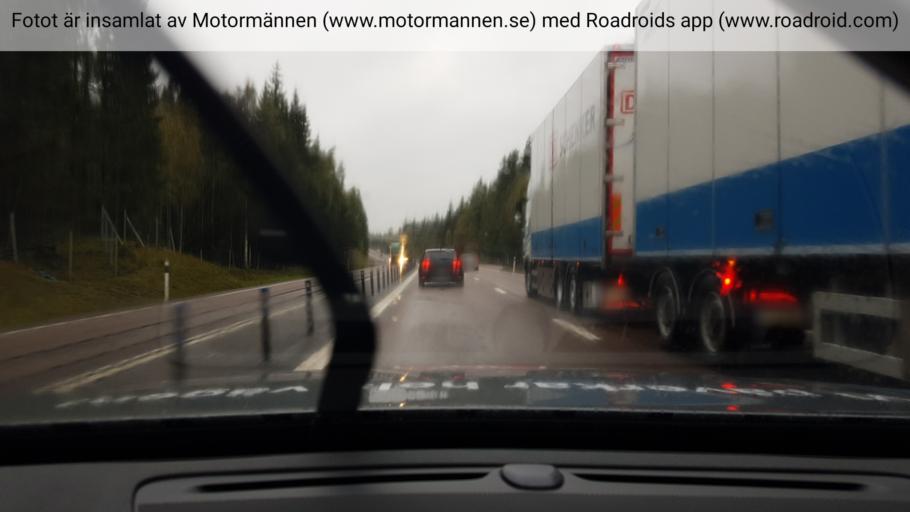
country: SE
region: Vaermland
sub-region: Kristinehamns Kommun
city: Bjorneborg
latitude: 59.3118
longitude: 14.2684
